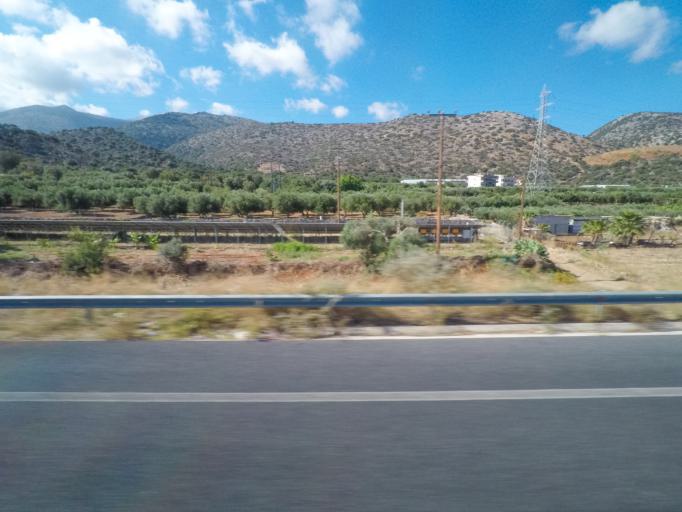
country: GR
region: Crete
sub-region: Nomos Irakleiou
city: Malia
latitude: 35.2806
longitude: 25.4800
